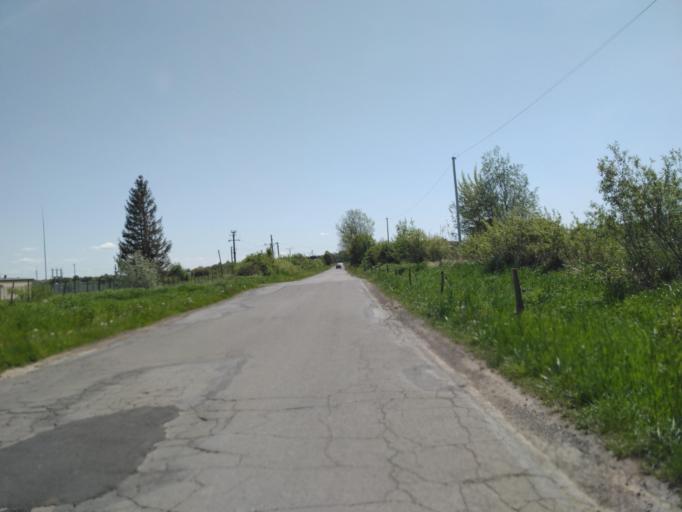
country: PL
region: Subcarpathian Voivodeship
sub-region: Powiat krosnienski
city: Miejsce Piastowe
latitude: 49.6068
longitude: 21.7802
